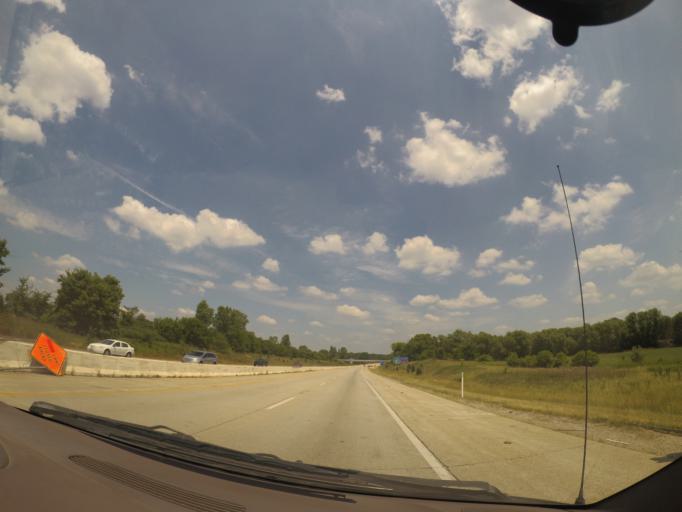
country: US
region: Indiana
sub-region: Saint Joseph County
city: Osceola
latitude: 41.6243
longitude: -86.0272
